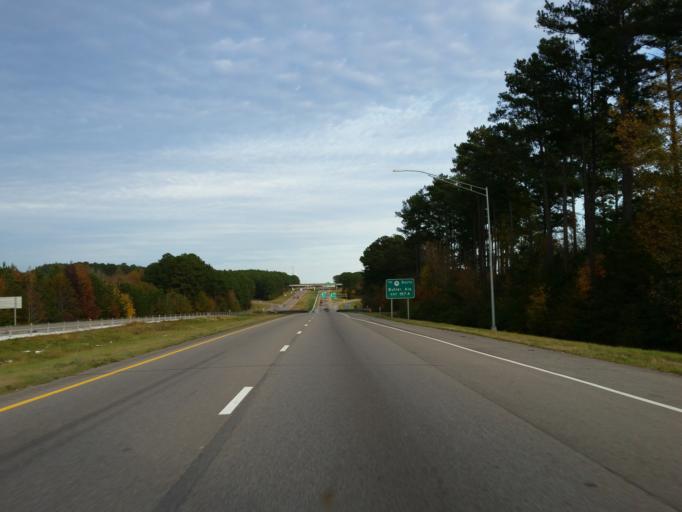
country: US
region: Mississippi
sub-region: Lauderdale County
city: Marion
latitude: 32.3811
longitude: -88.6474
